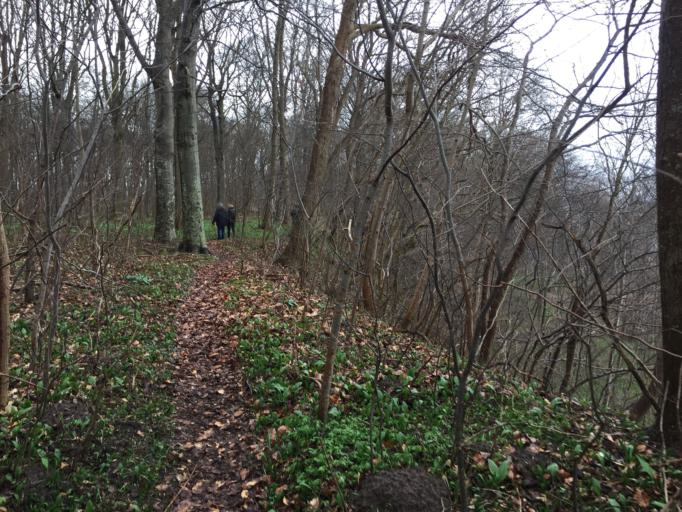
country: DK
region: South Denmark
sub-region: Assens Kommune
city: Harby
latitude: 55.1455
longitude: 10.0289
